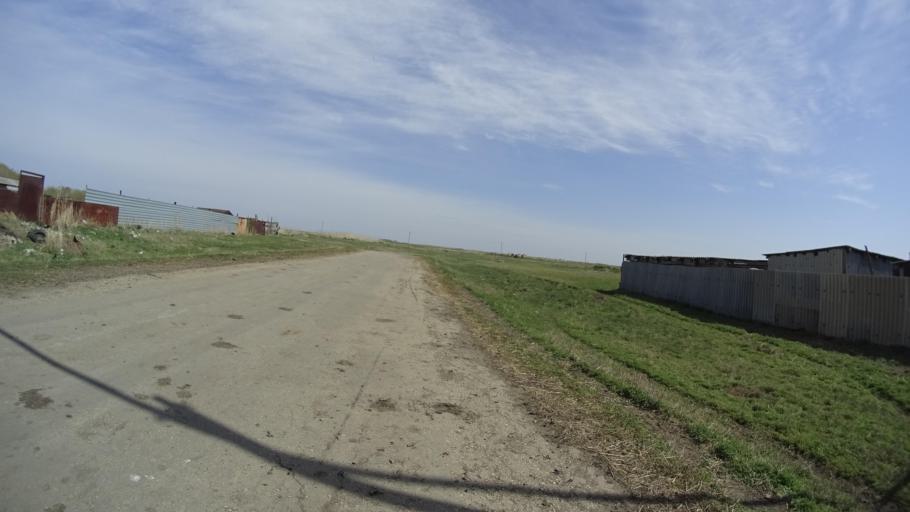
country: RU
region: Chelyabinsk
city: Chesma
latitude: 53.8006
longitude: 61.0219
